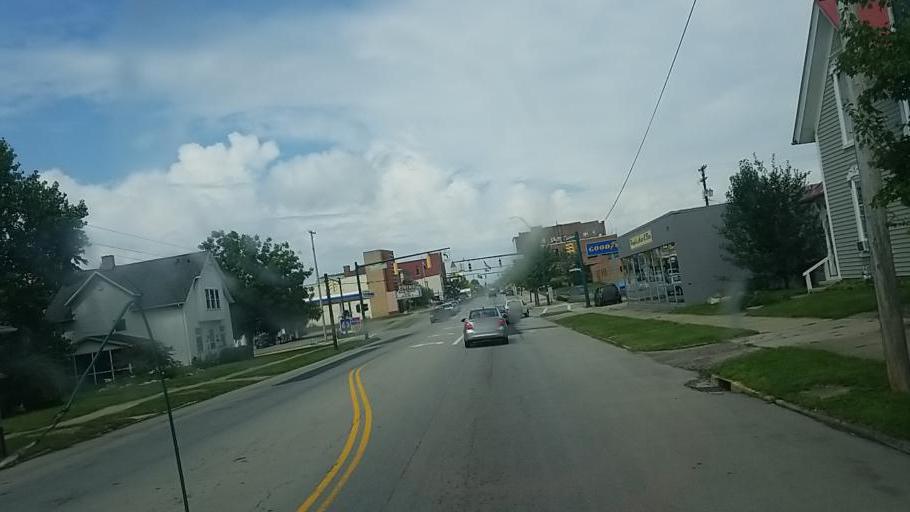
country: US
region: Ohio
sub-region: Champaign County
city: Urbana
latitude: 40.1049
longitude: -83.7528
